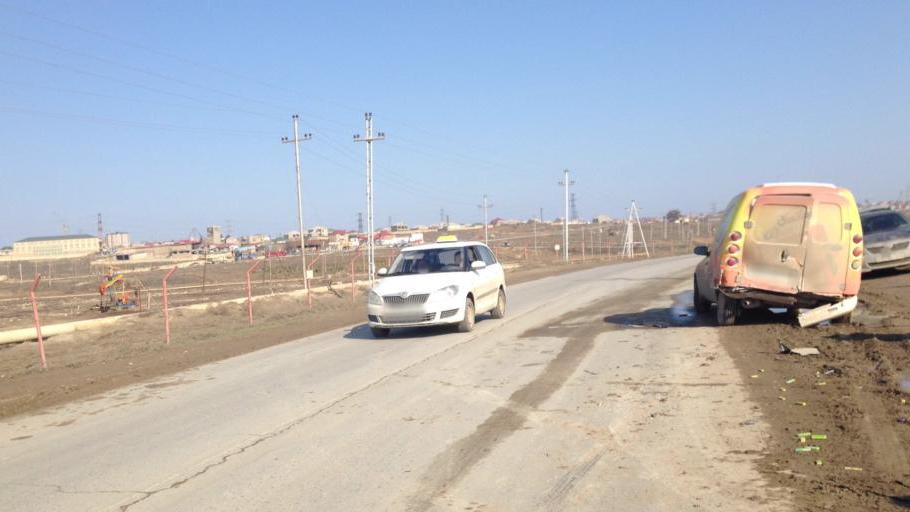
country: AZ
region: Abseron
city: Digah
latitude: 40.4763
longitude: 49.8538
